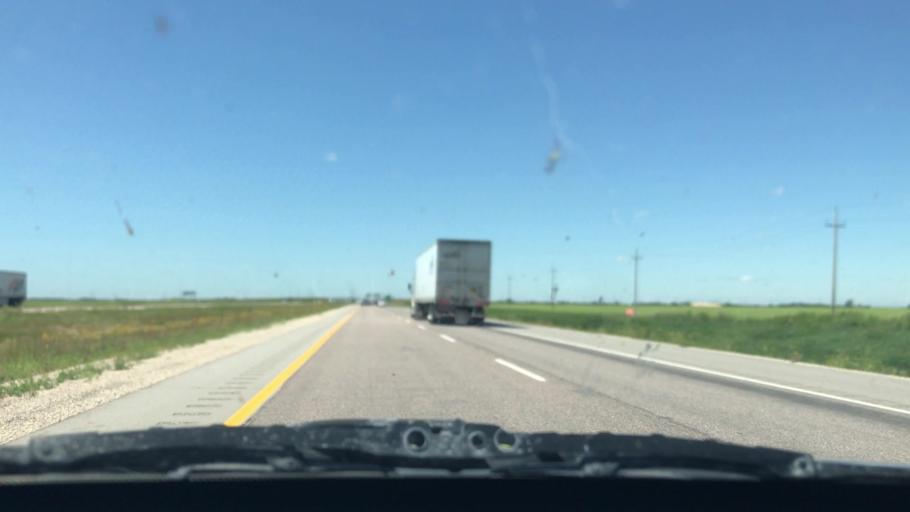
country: CA
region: Manitoba
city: Steinbach
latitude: 49.6937
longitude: -96.6273
